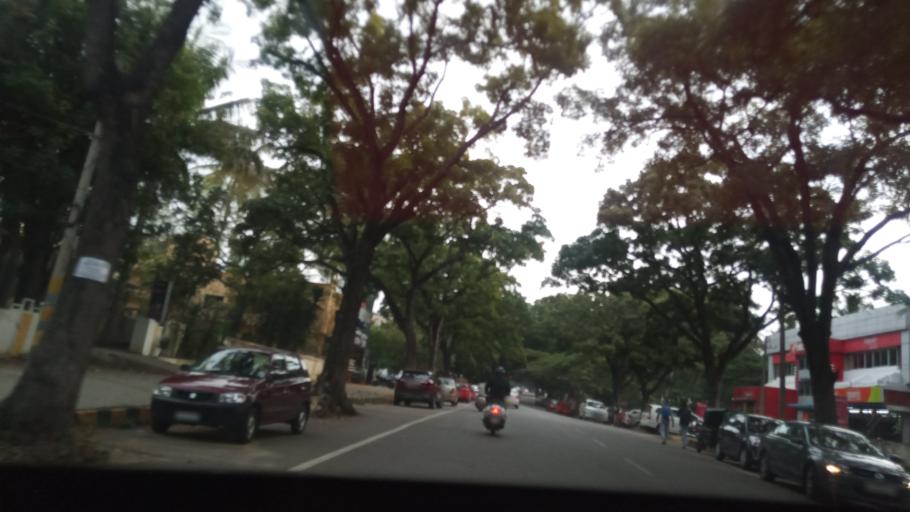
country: IN
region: Karnataka
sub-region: Mysore
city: Mysore
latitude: 12.3282
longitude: 76.6311
